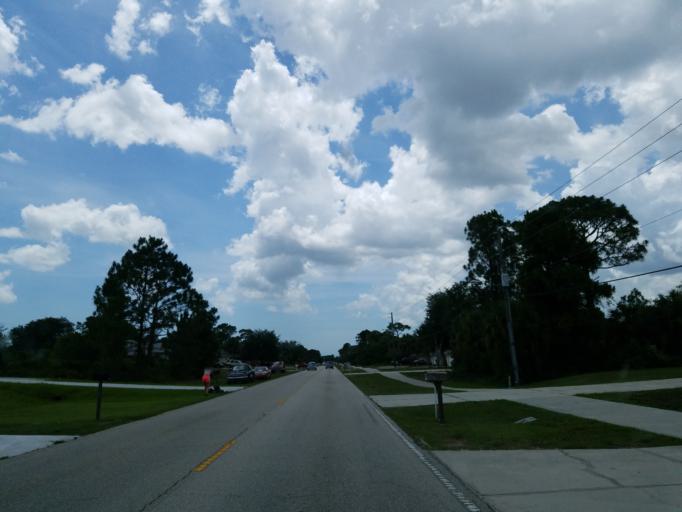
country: US
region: Florida
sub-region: Sarasota County
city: North Port
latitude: 27.0688
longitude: -82.1874
